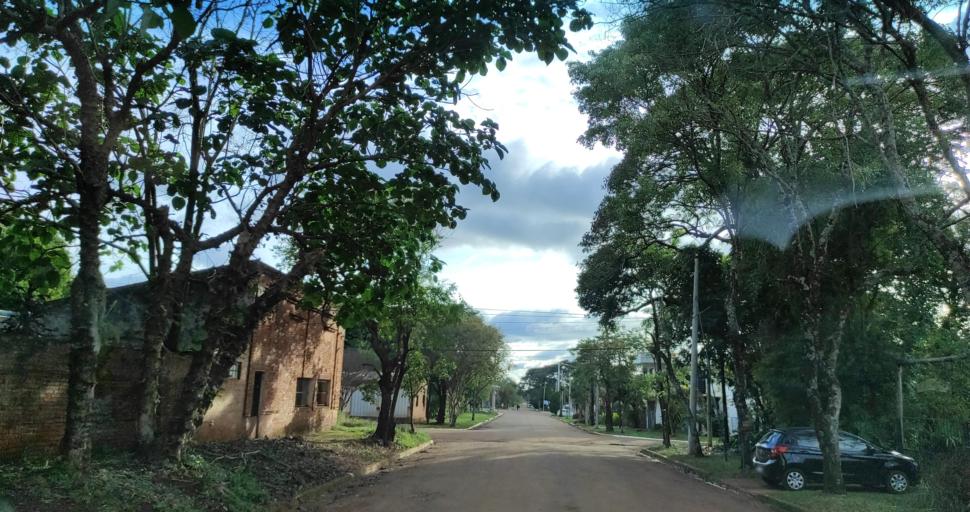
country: AR
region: Misiones
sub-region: Departamento de Candelaria
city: Candelaria
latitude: -27.4597
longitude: -55.7428
